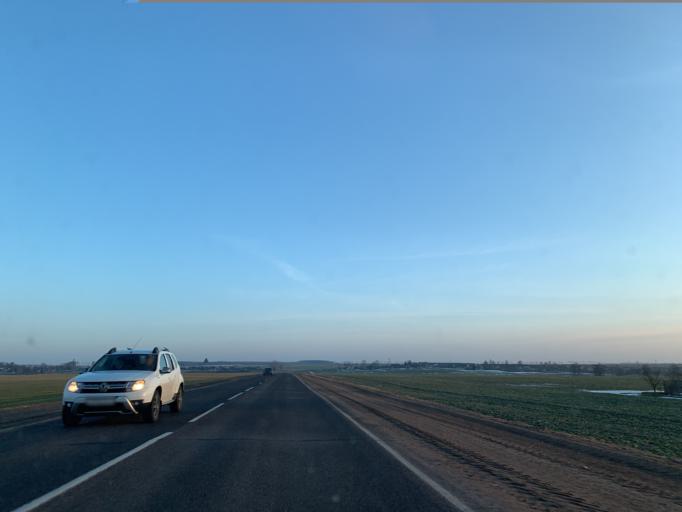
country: BY
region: Minsk
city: Haradzyeya
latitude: 53.3102
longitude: 26.5674
